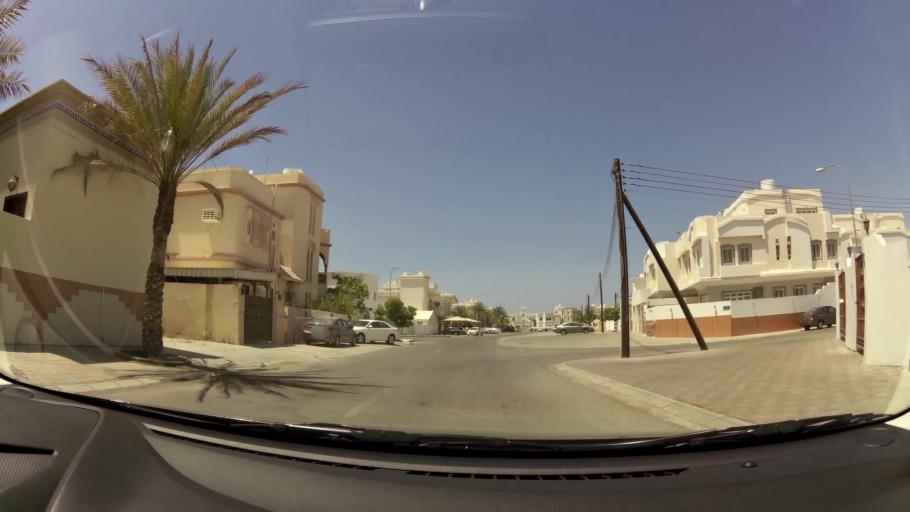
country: OM
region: Muhafazat Masqat
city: Bawshar
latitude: 23.5918
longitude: 58.3793
